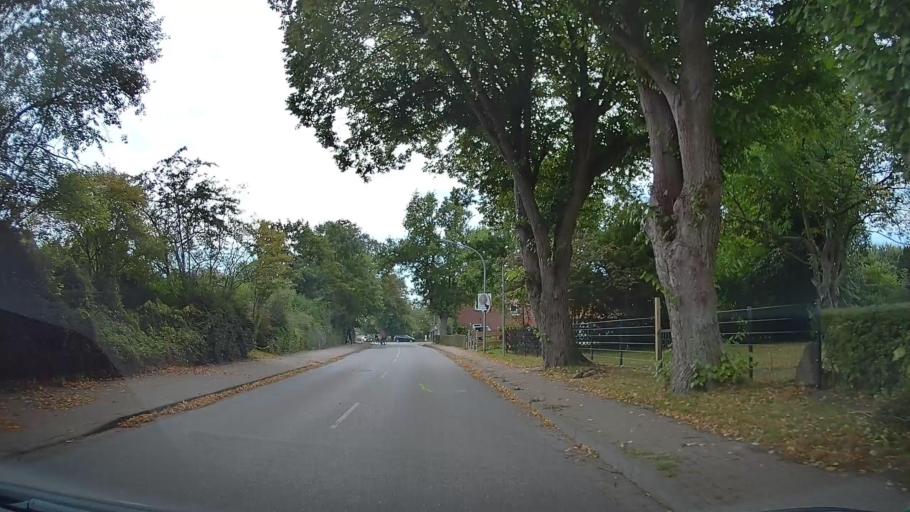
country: DE
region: Schleswig-Holstein
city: Panker
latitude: 54.3475
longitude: 10.6038
